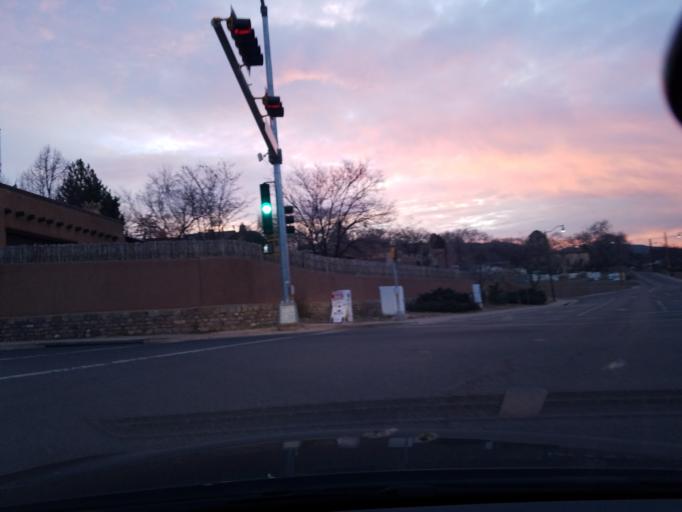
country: US
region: New Mexico
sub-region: Santa Fe County
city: Santa Fe
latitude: 35.6912
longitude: -105.9365
